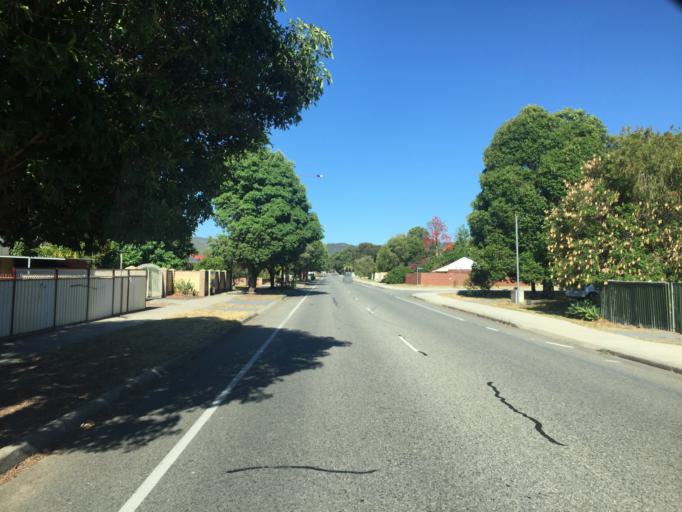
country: AU
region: Western Australia
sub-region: Gosnells
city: Gosnells
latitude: -32.0631
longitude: 116.0012
